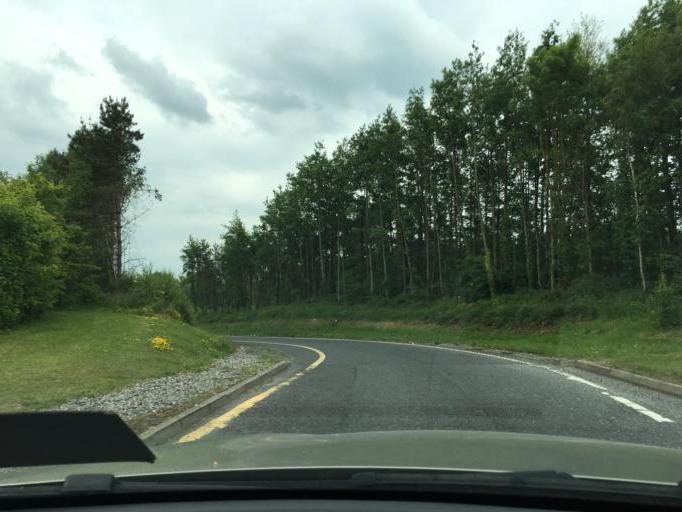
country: IE
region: Leinster
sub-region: Kildare
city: Athgarvan
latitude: 53.1628
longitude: -6.8238
